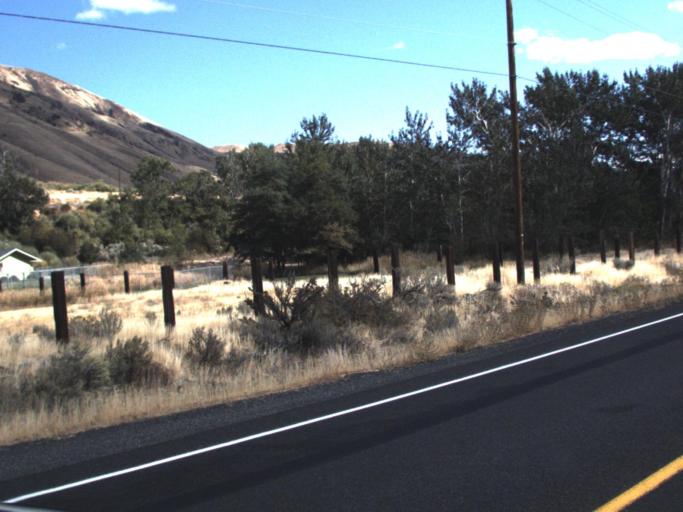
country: US
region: Washington
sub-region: Yakima County
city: Tieton
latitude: 46.7471
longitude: -120.7703
